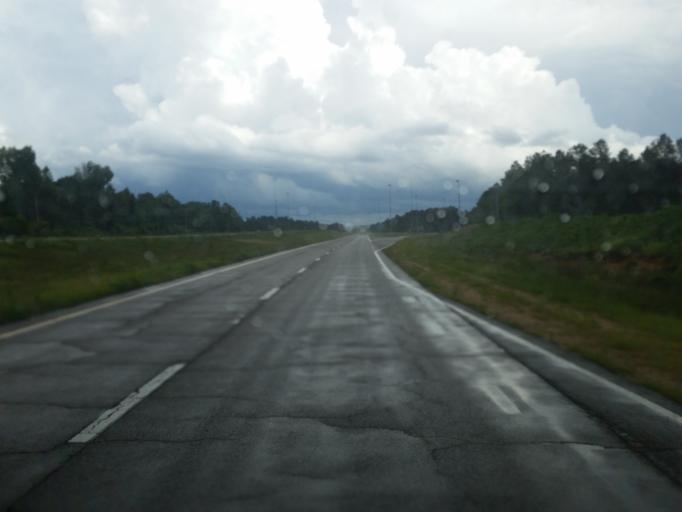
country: US
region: Mississippi
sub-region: George County
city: Lucedale
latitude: 30.8938
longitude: -88.4511
